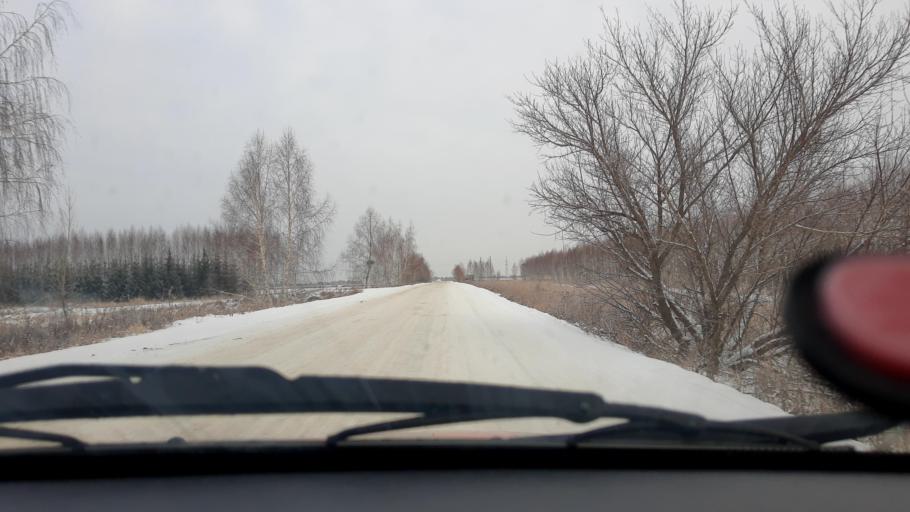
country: RU
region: Bashkortostan
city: Iglino
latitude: 54.7496
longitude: 56.2833
